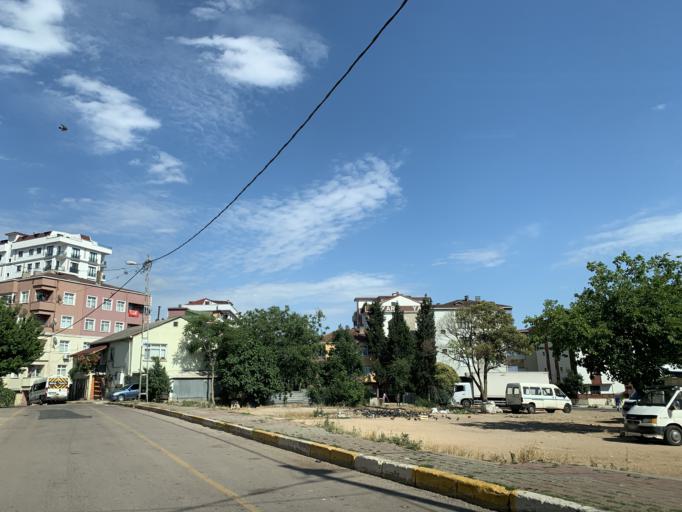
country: TR
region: Istanbul
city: Pendik
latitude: 40.8863
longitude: 29.2691
